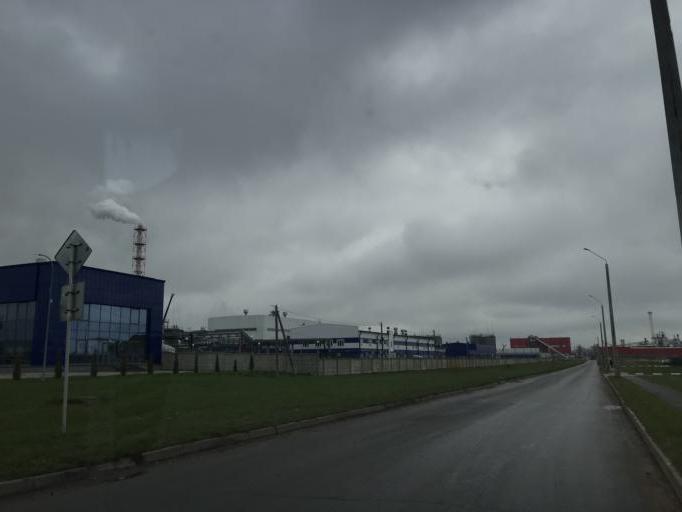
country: BY
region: Mogilev
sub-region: Mahilyowski Rayon
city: Veyno
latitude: 53.8286
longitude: 30.3525
